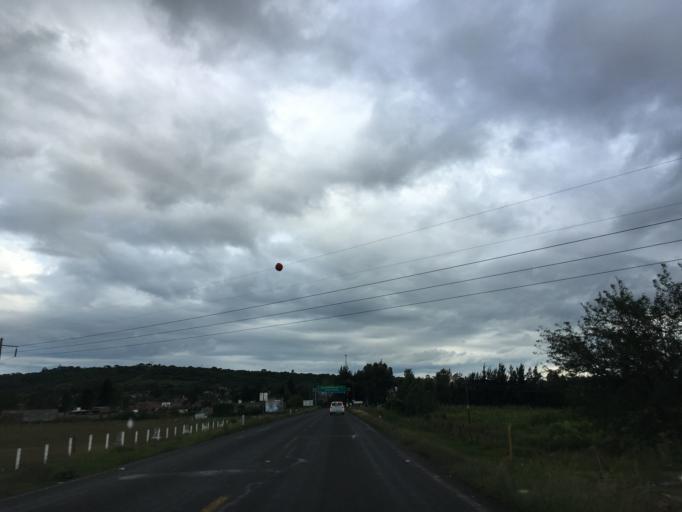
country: MX
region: Michoacan
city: Cuitzeo del Porvenir
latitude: 19.9760
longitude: -101.1411
